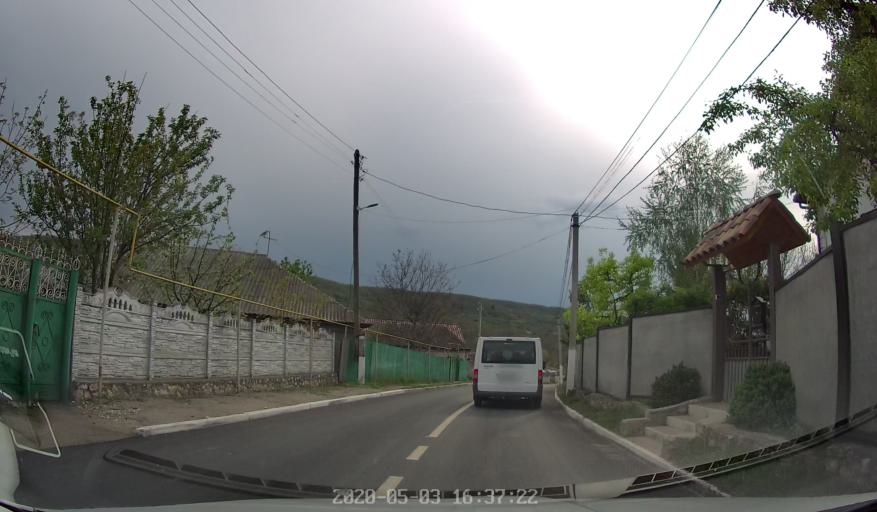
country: MD
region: Calarasi
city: Calarasi
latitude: 47.1915
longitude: 28.3560
